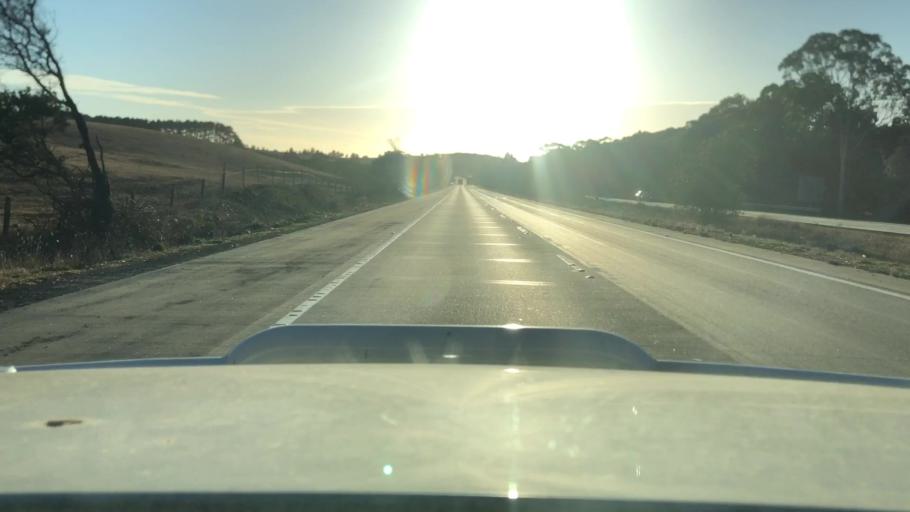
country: AU
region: New South Wales
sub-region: Wingecarribee
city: Bundanoon
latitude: -34.6878
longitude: 150.0430
